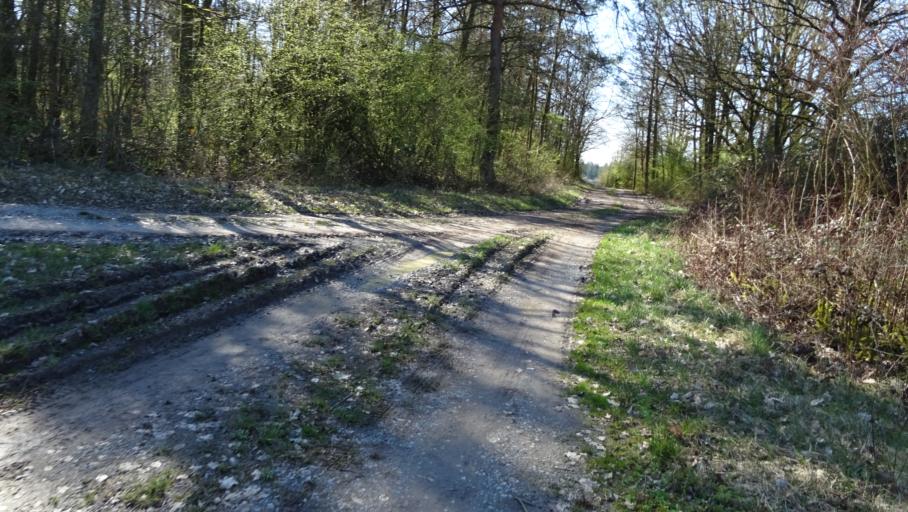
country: DE
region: Baden-Wuerttemberg
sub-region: Karlsruhe Region
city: Seckach
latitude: 49.4287
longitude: 9.3179
